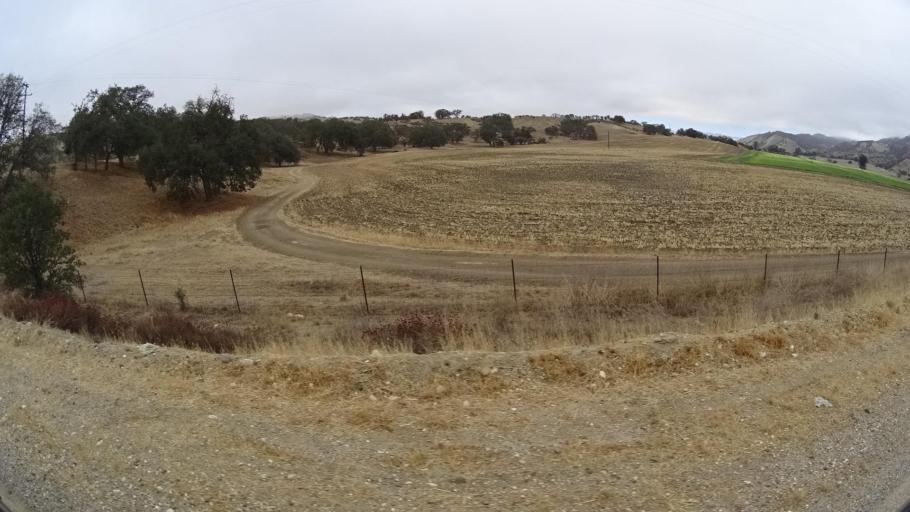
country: US
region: California
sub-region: San Luis Obispo County
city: San Miguel
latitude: 35.9055
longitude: -120.6990
